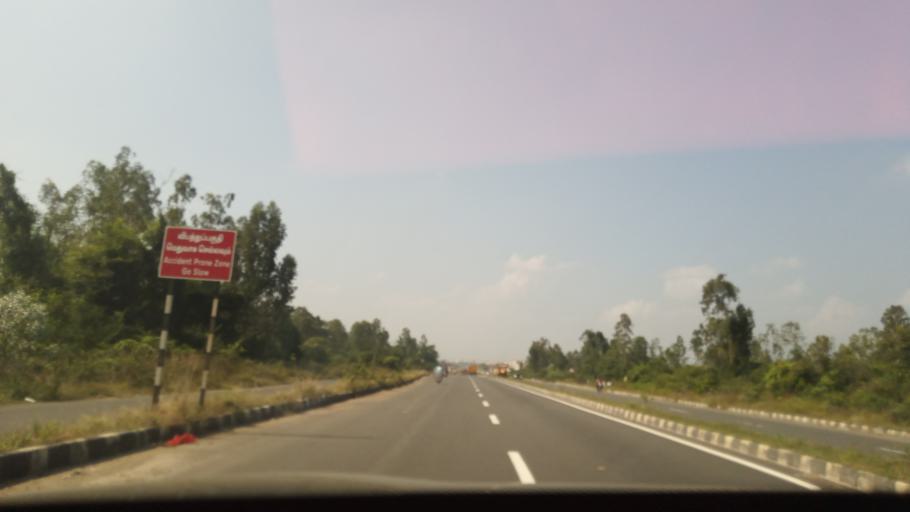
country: IN
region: Tamil Nadu
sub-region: Kancheepuram
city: Madambakkam
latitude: 12.8573
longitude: 79.9553
